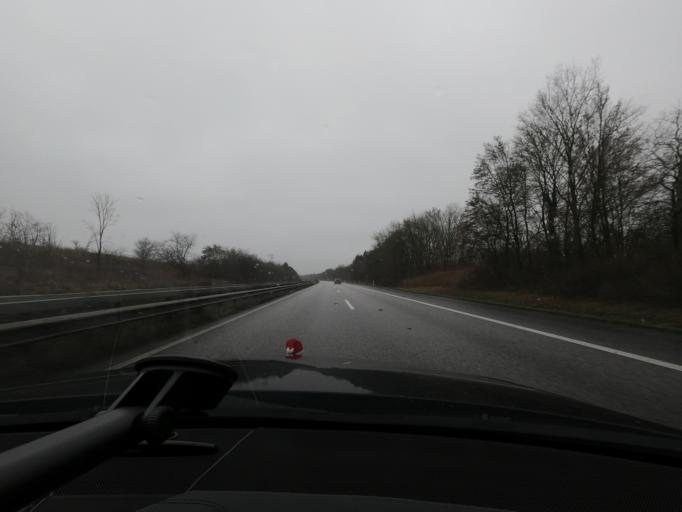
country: DE
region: Schleswig-Holstein
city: Eisendorf
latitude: 54.2056
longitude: 9.8723
